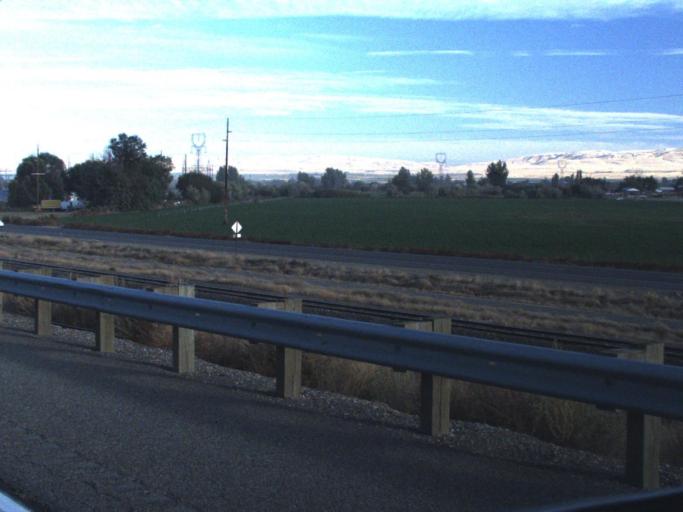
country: US
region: Washington
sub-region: Yakima County
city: Grandview
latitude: 46.2891
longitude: -119.9488
